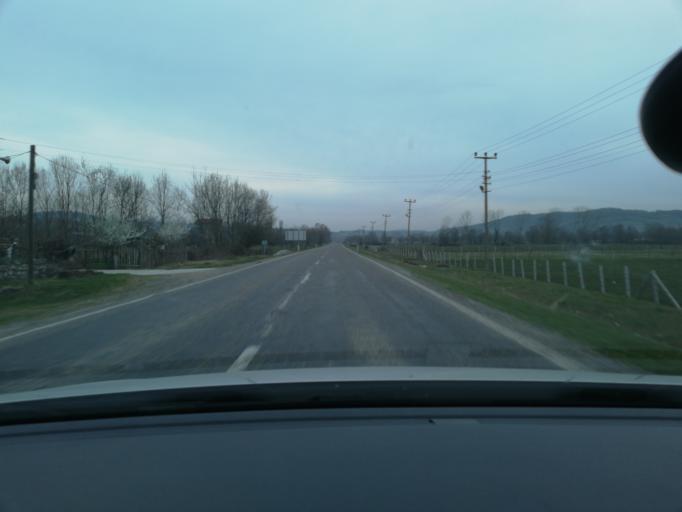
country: TR
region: Zonguldak
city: Saltukova
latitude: 41.5051
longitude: 32.0991
